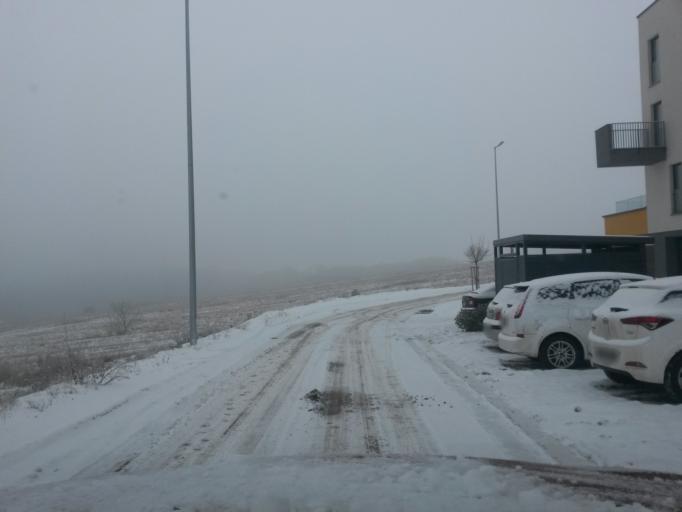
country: SK
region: Kosicky
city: Kosice
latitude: 48.7275
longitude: 21.2968
